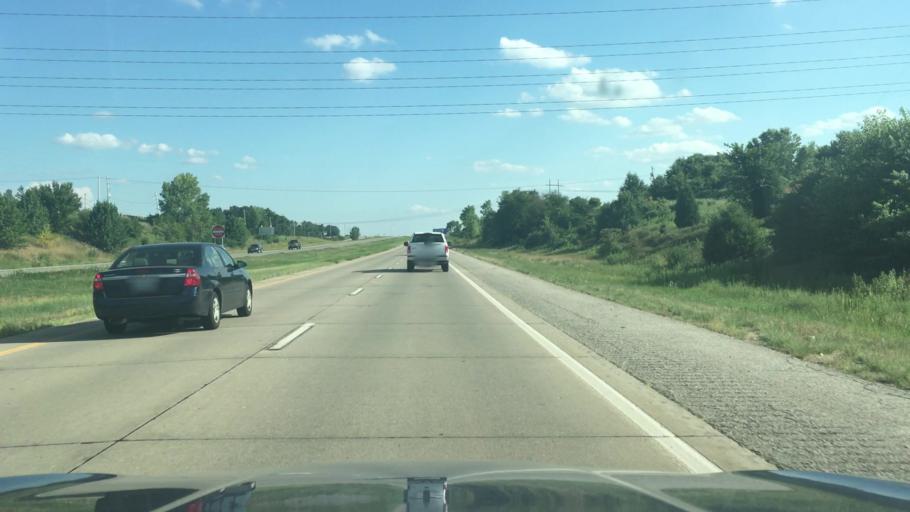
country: US
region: Missouri
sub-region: Jackson County
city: Greenwood
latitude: 38.8665
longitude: -94.3752
